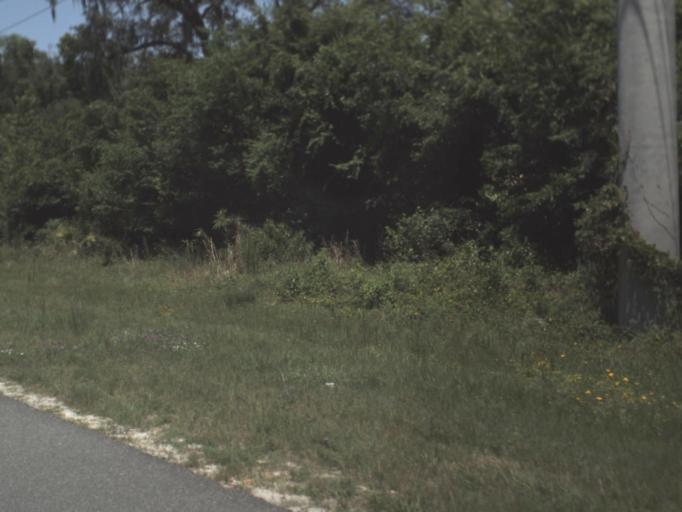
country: US
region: Florida
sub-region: Levy County
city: Manatee Road
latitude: 29.6358
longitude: -82.9835
